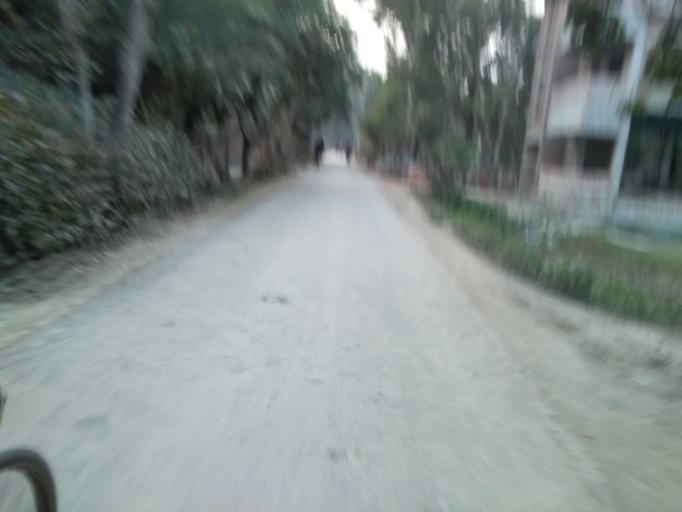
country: IN
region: West Bengal
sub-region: North 24 Parganas
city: Taki
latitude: 22.6508
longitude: 88.9998
